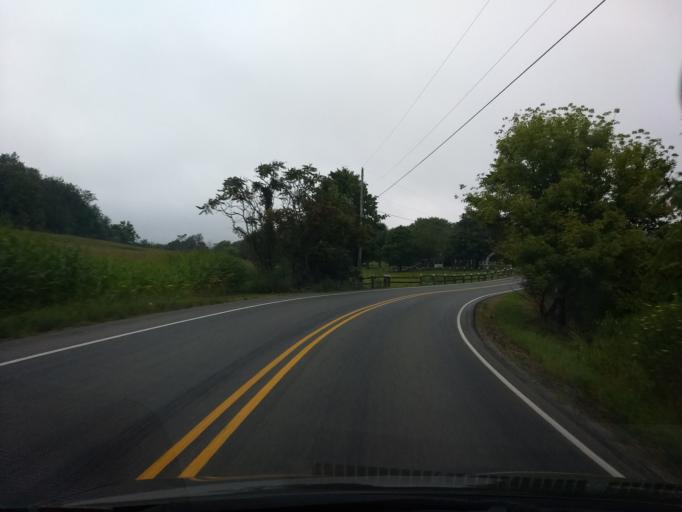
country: US
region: Pennsylvania
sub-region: Westmoreland County
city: Greensburg
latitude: 40.3309
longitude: -79.4872
